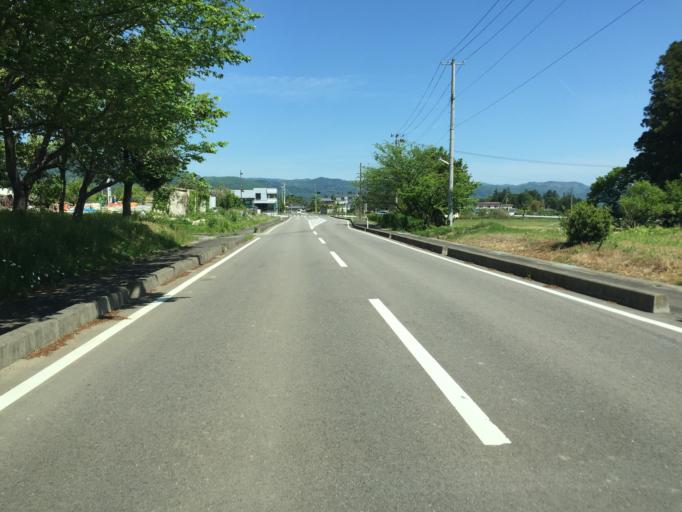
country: JP
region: Fukushima
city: Fukushima-shi
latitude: 37.7208
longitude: 140.3779
